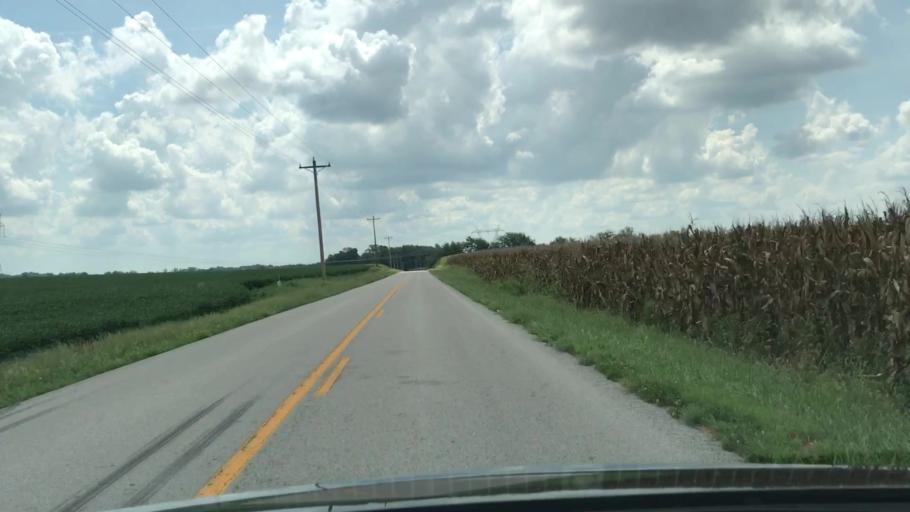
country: US
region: Kentucky
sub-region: Todd County
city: Elkton
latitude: 36.7773
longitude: -87.1196
